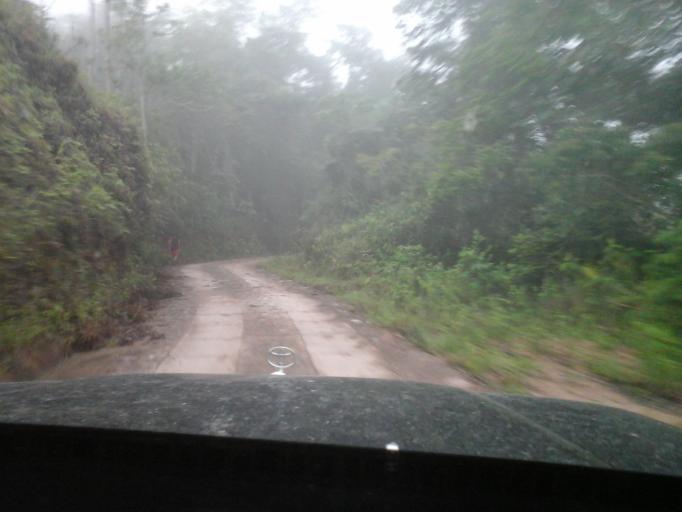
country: CO
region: Cesar
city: Agustin Codazzi
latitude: 9.9390
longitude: -73.1419
